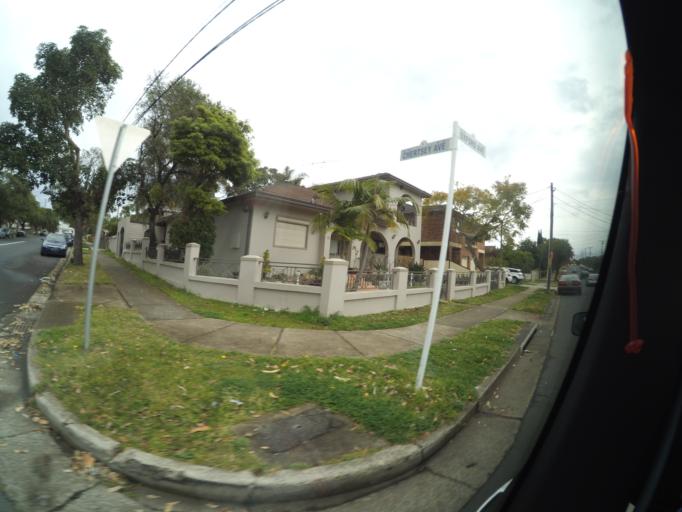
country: AU
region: New South Wales
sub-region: Bankstown
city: Bankstown
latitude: -33.9232
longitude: 151.0252
